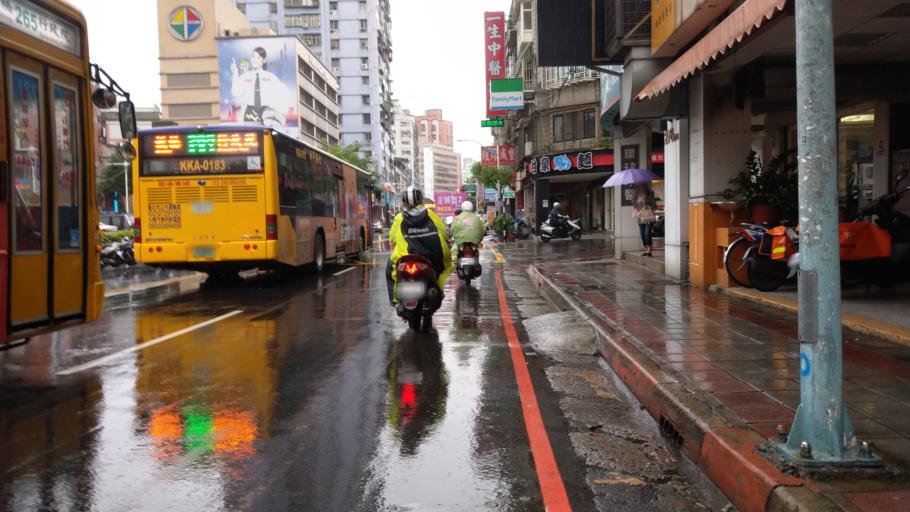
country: TW
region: Taipei
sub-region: Taipei
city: Banqiao
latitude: 25.0000
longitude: 121.4630
